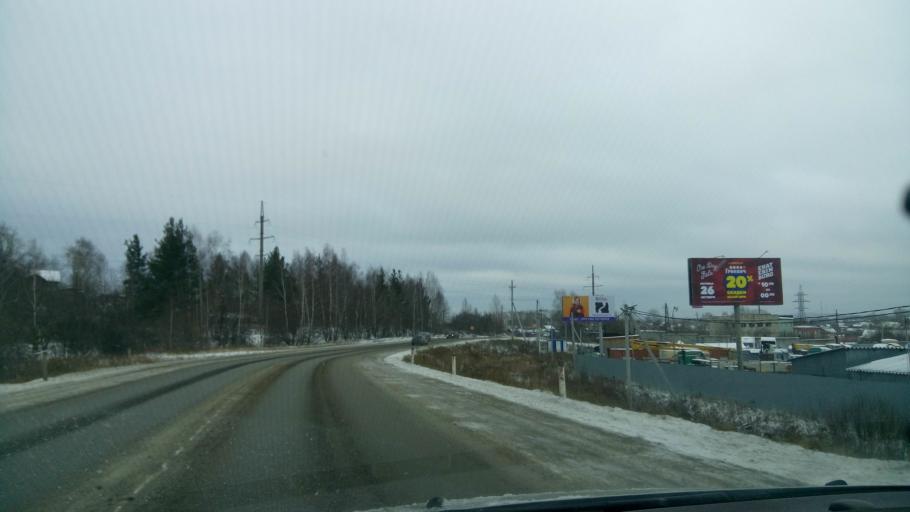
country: RU
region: Sverdlovsk
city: Polevskoy
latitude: 56.4594
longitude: 60.2135
